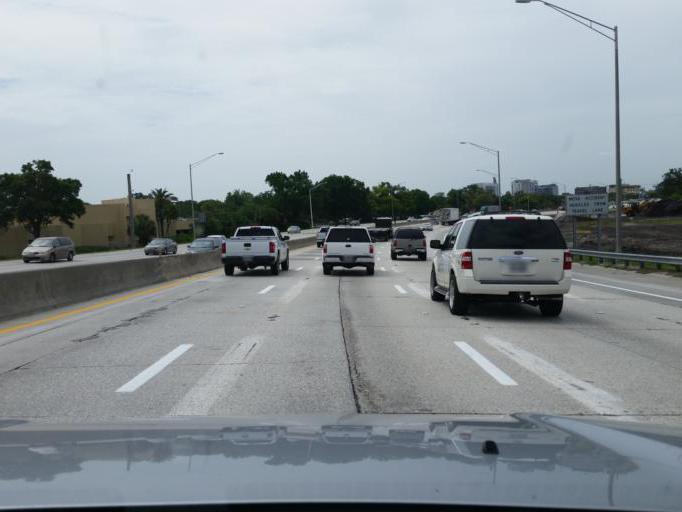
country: US
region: Florida
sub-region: Orange County
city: Fairview Shores
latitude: 28.5880
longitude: -81.3764
